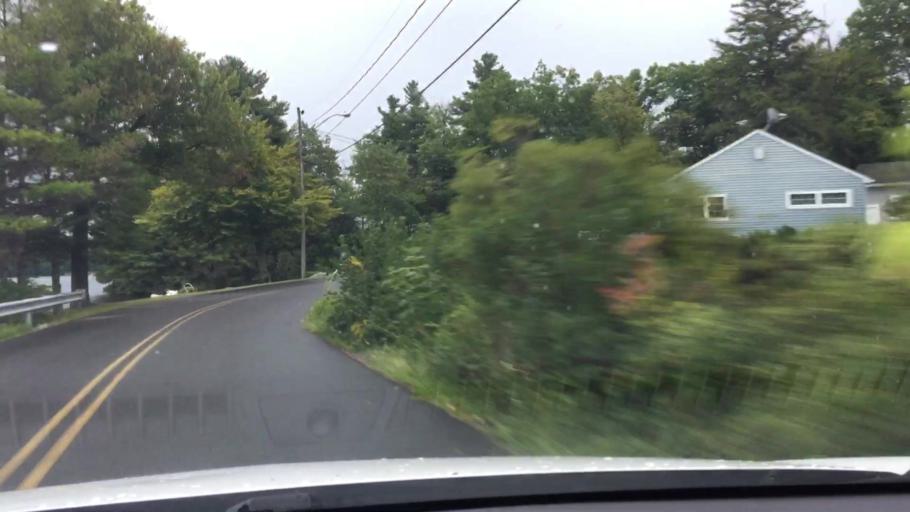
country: US
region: Massachusetts
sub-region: Berkshire County
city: Otis
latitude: 42.1523
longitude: -73.0570
